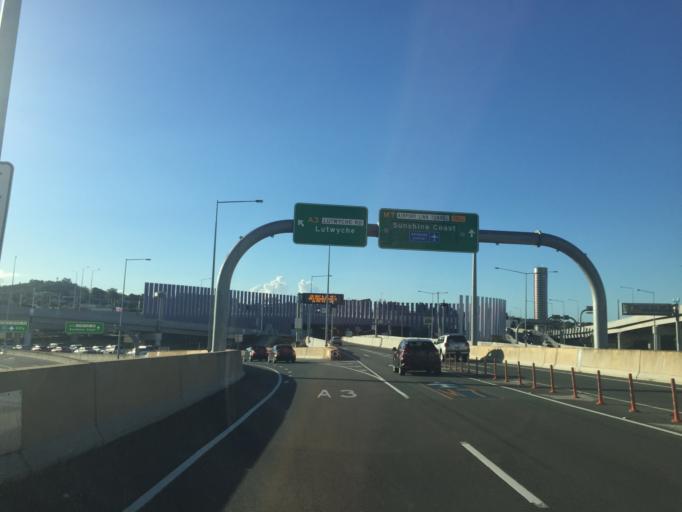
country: AU
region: Queensland
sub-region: Brisbane
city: Windsor
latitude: -27.4442
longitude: 153.0314
